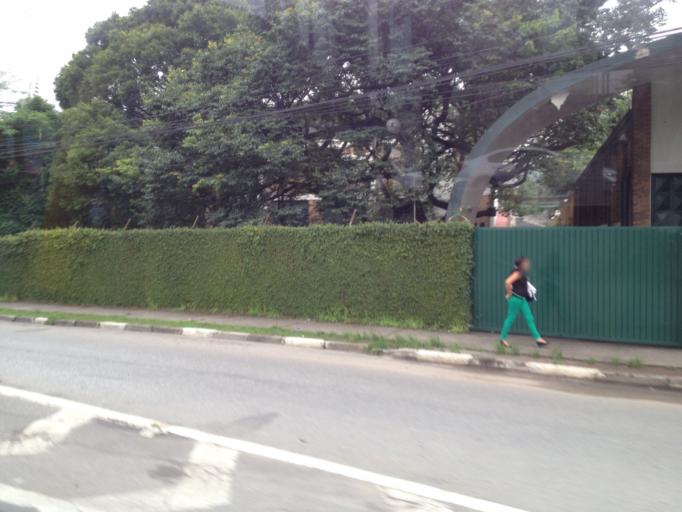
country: BR
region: Sao Paulo
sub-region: Taboao Da Serra
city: Taboao da Serra
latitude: -23.6447
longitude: -46.7244
